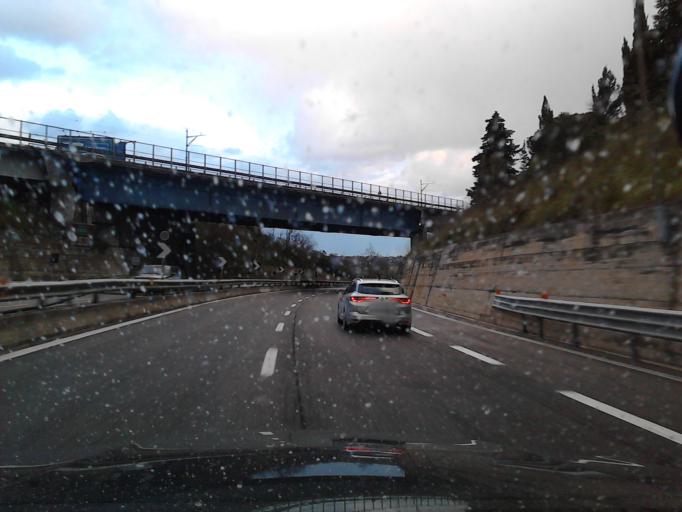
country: IT
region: Abruzzo
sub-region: Provincia di Chieti
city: Treglio
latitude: 42.2695
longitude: 14.4344
